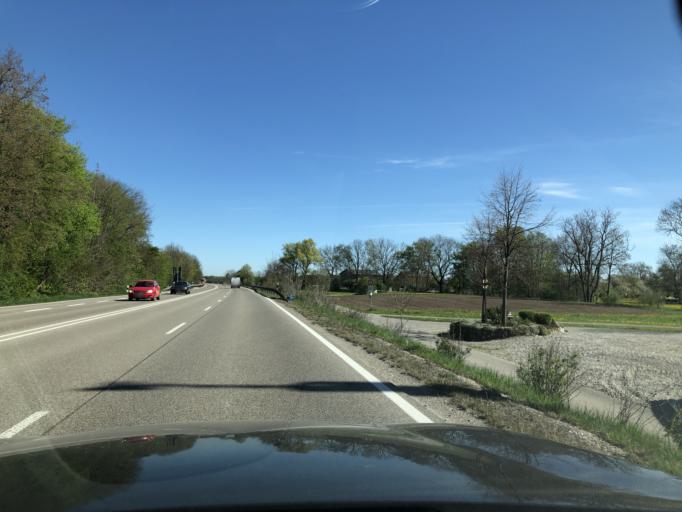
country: DE
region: Bavaria
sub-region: Swabia
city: Jengen
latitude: 48.0054
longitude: 10.7214
